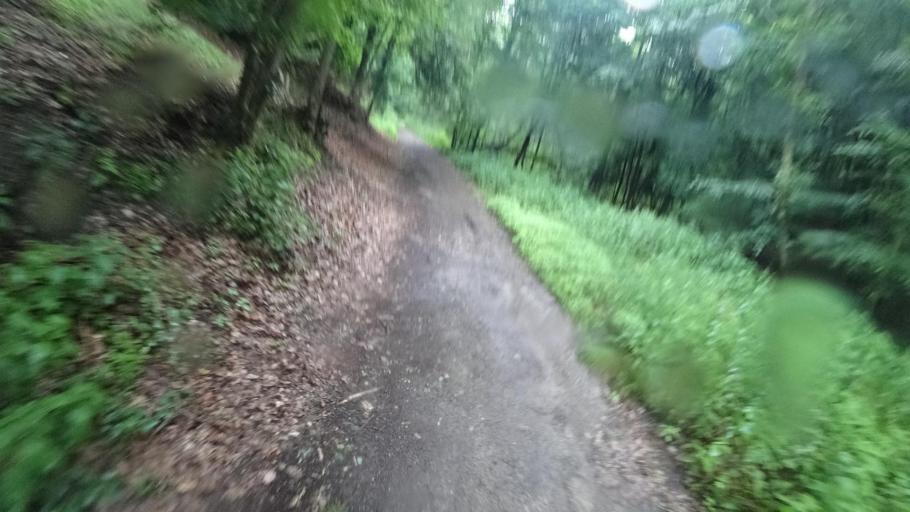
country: DE
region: Rheinland-Pfalz
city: Dernau
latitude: 50.5452
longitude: 7.0664
